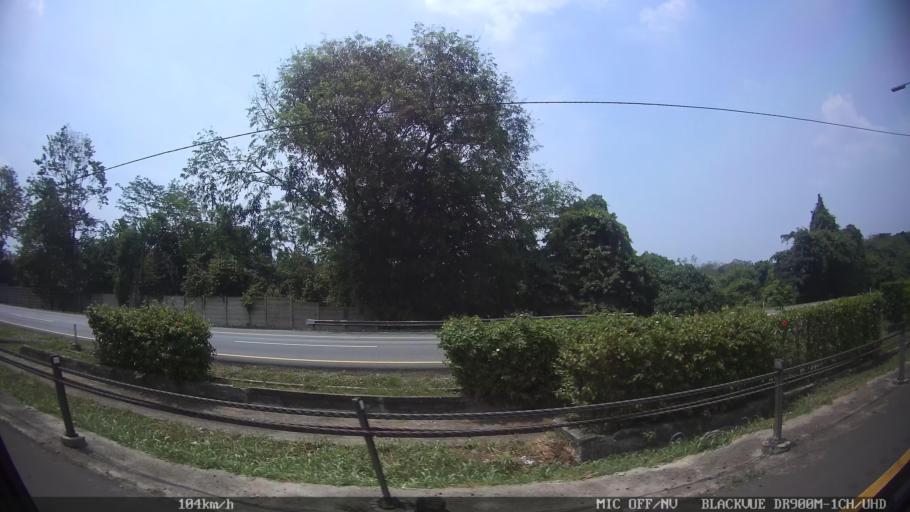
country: ID
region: Banten
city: Serang
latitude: -6.0877
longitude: 106.1431
